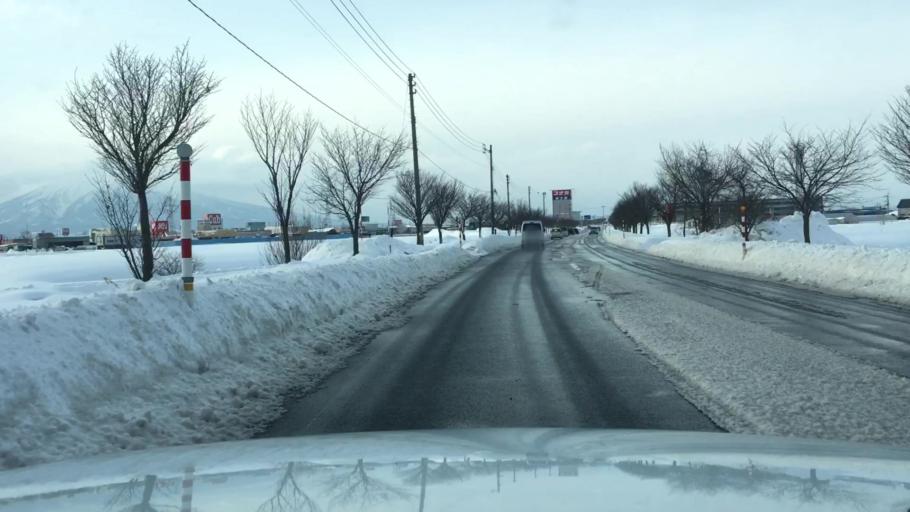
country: JP
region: Aomori
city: Hirosaki
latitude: 40.5951
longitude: 140.5180
